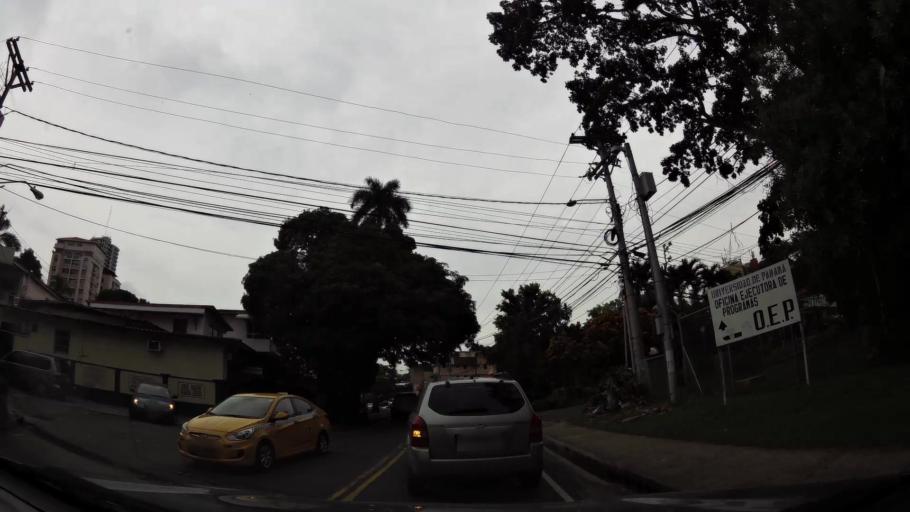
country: PA
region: Panama
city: Panama
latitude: 8.9831
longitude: -79.5314
